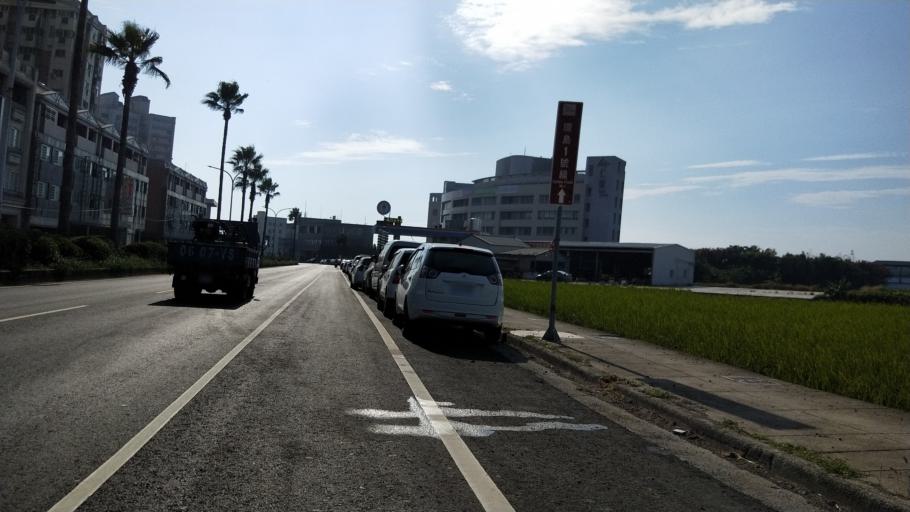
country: TW
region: Taiwan
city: Fengyuan
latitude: 24.3566
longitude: 120.6220
